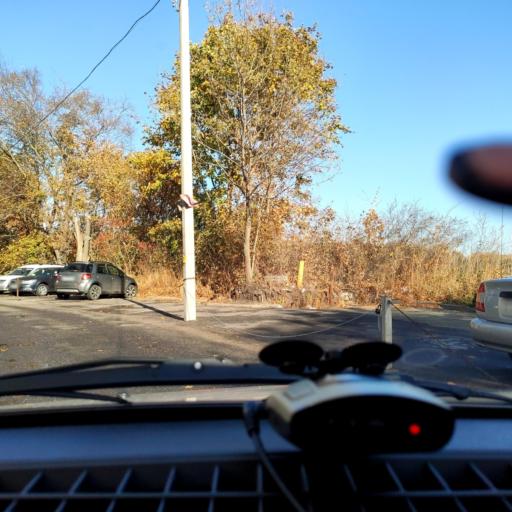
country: RU
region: Voronezj
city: Voronezh
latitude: 51.7043
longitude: 39.2229
